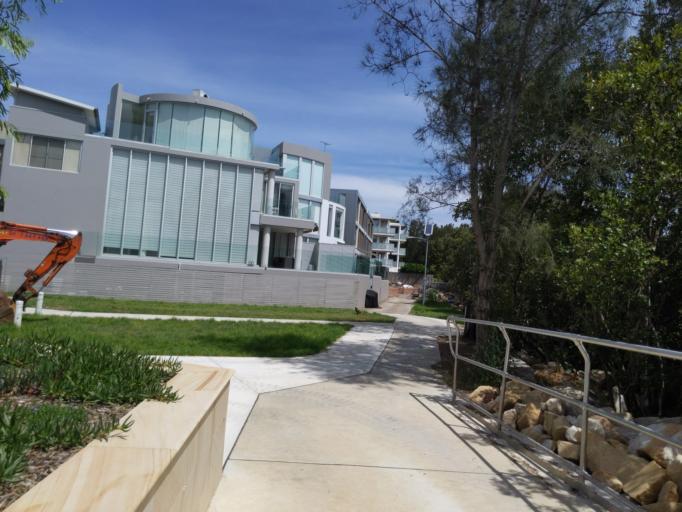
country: AU
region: New South Wales
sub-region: Canada Bay
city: Concord
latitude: -33.8403
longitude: 151.1050
